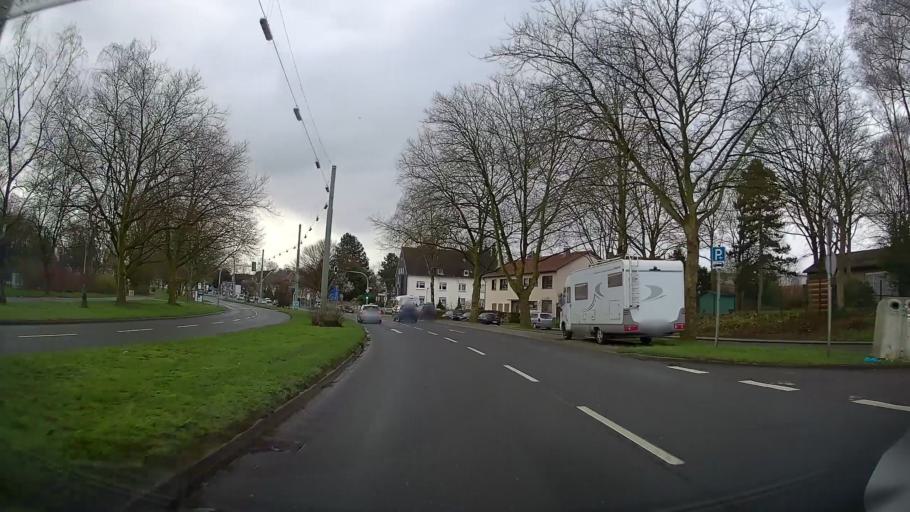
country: DE
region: North Rhine-Westphalia
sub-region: Regierungsbezirk Arnsberg
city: Herne
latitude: 51.5506
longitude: 7.2077
